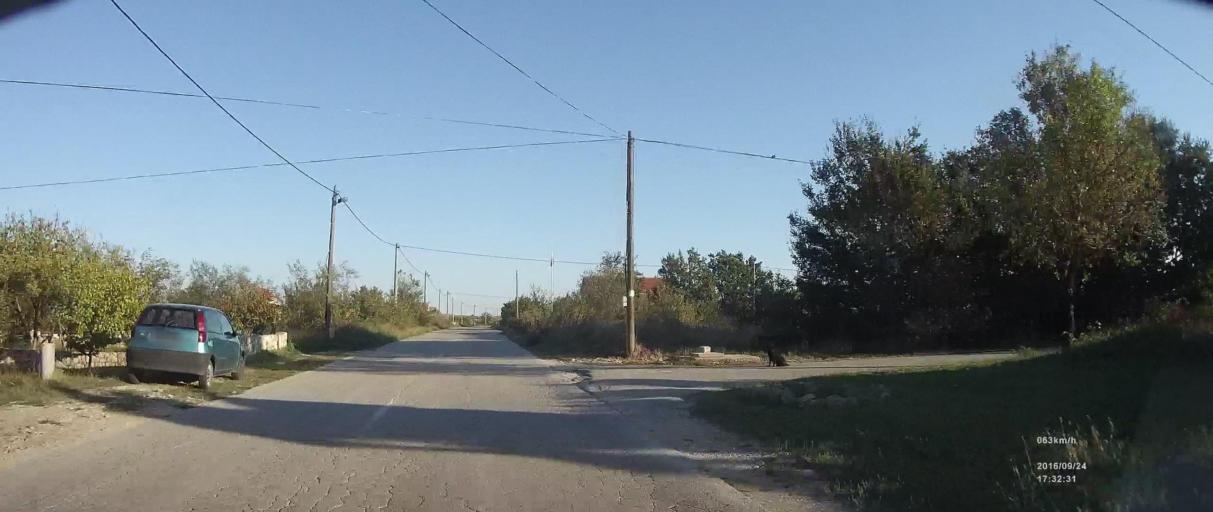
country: HR
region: Zadarska
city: Posedarje
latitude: 44.1816
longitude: 15.4509
